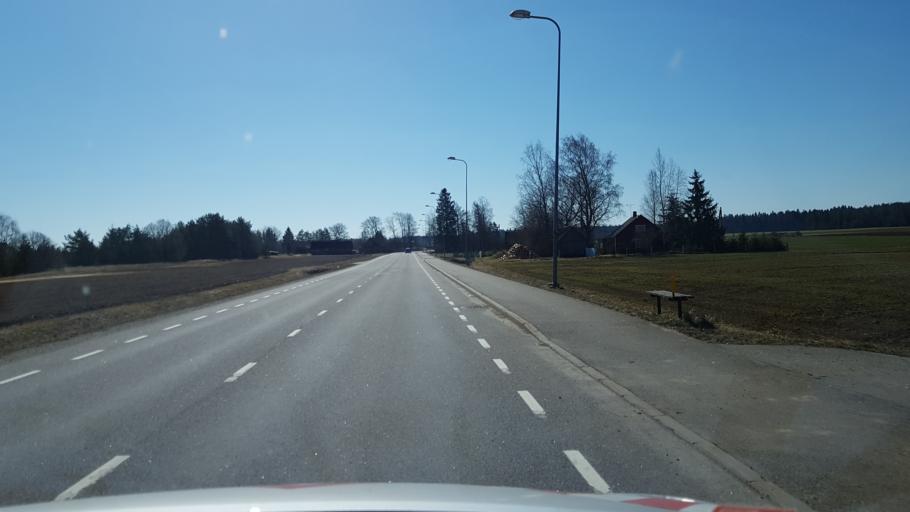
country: EE
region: Laeaene-Virumaa
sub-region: Vinni vald
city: Vinni
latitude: 59.1527
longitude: 26.5921
